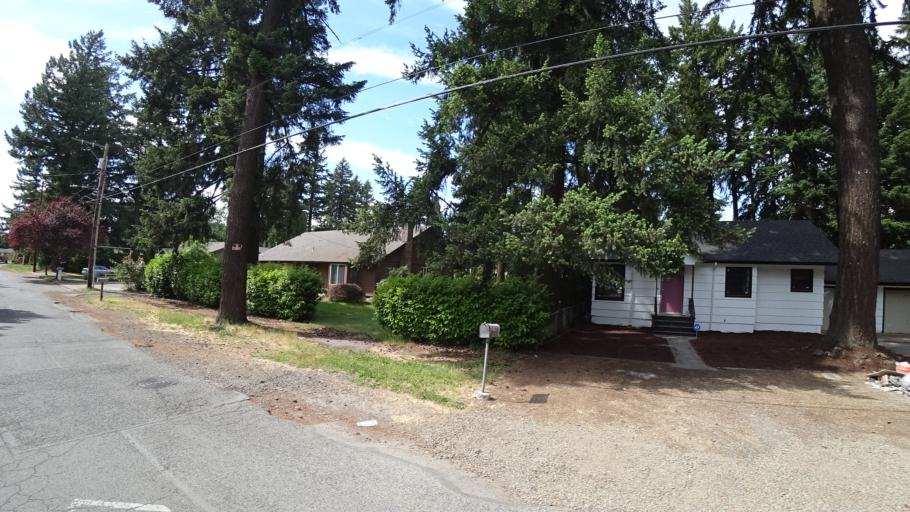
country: US
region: Oregon
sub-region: Multnomah County
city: Lents
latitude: 45.4945
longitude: -122.5421
